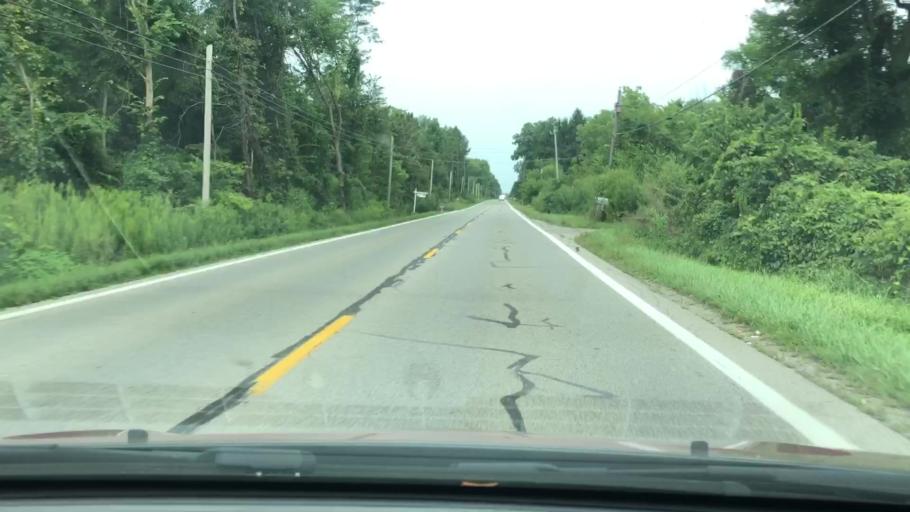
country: US
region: Ohio
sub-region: Delaware County
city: Sunbury
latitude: 40.2241
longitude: -82.8163
